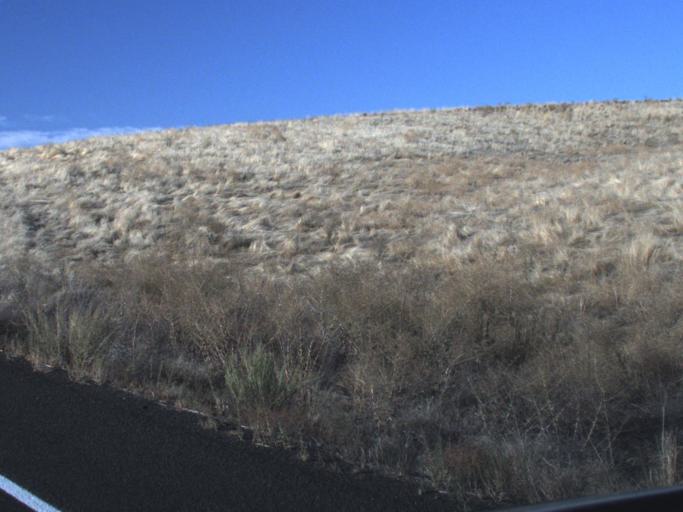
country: US
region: Washington
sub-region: Walla Walla County
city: Garrett
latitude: 46.2907
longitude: -118.5565
